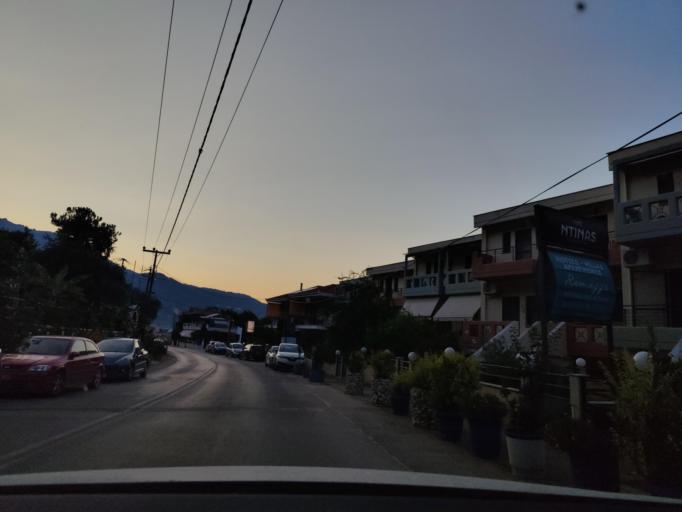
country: GR
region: East Macedonia and Thrace
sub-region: Nomos Kavalas
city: Potamia
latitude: 40.7061
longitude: 24.7613
